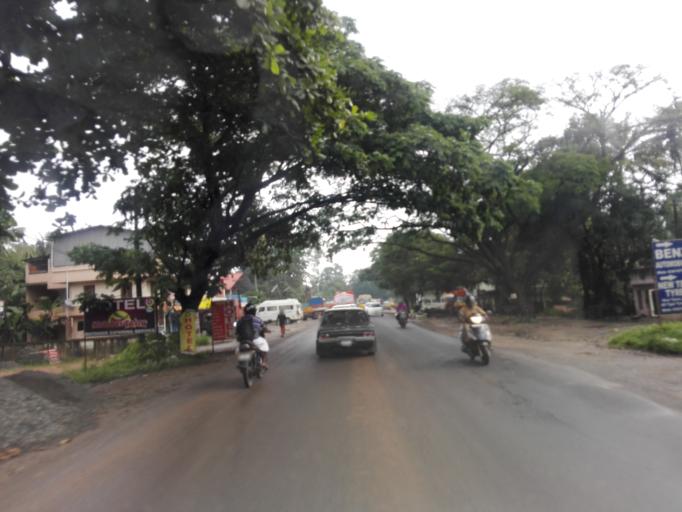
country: IN
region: Kerala
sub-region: Ernakulam
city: Cochin
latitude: 9.9751
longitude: 76.3546
